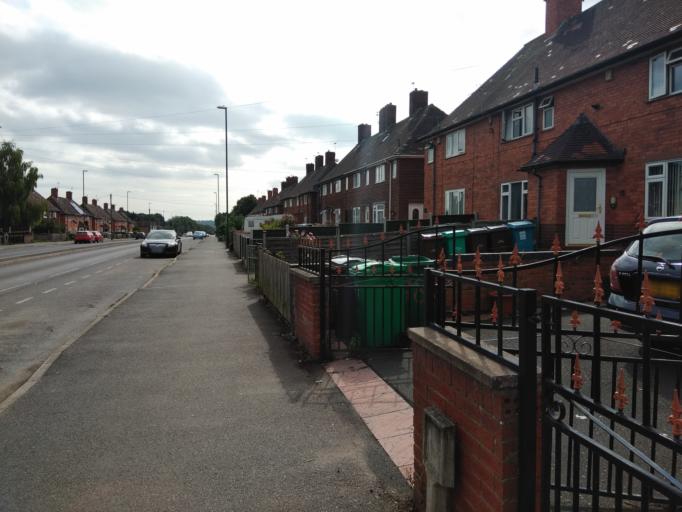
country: GB
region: England
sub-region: Nottinghamshire
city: Kimberley
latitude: 52.9700
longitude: -1.2136
